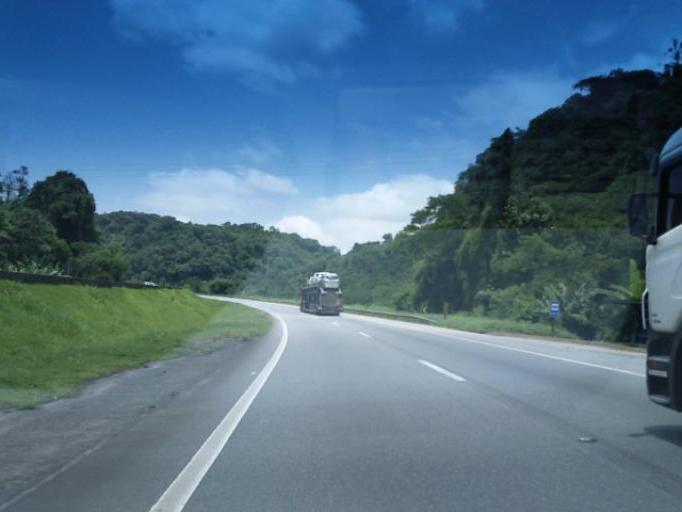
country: BR
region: Sao Paulo
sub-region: Miracatu
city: Miracatu
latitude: -24.1860
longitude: -47.3596
